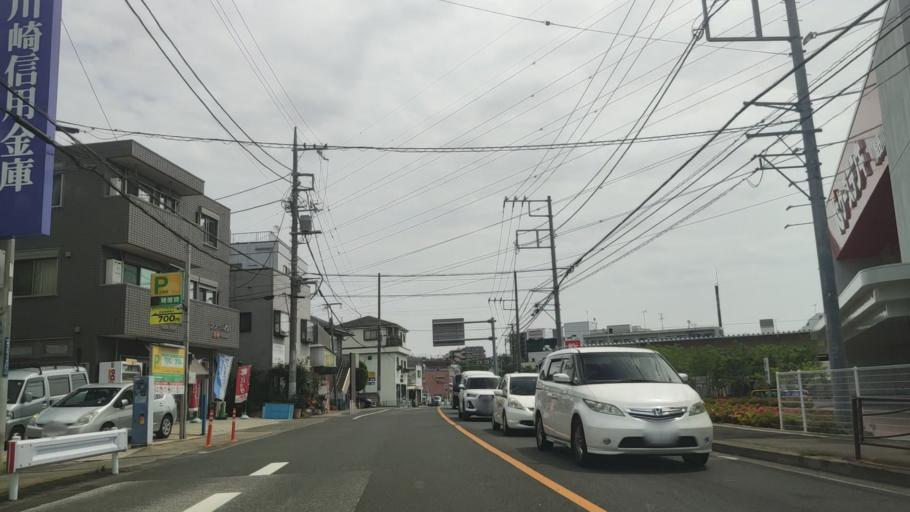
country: JP
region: Tokyo
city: Chofugaoka
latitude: 35.5735
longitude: 139.6183
